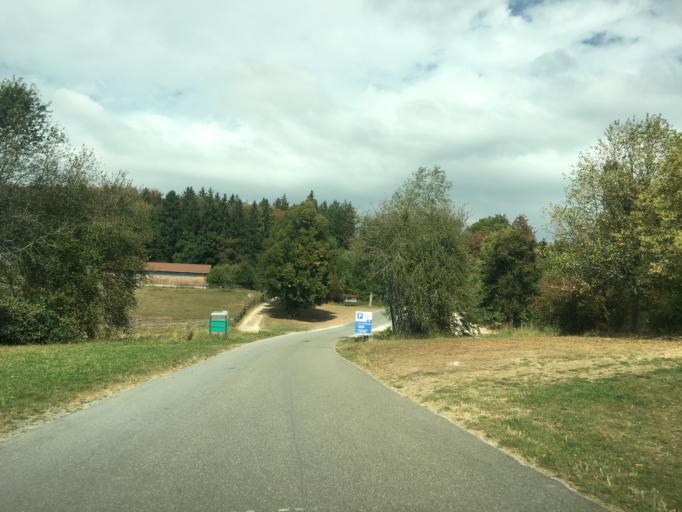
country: DE
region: Baden-Wuerttemberg
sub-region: Tuebingen Region
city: Trochtelfingen
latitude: 48.3672
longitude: 9.2206
